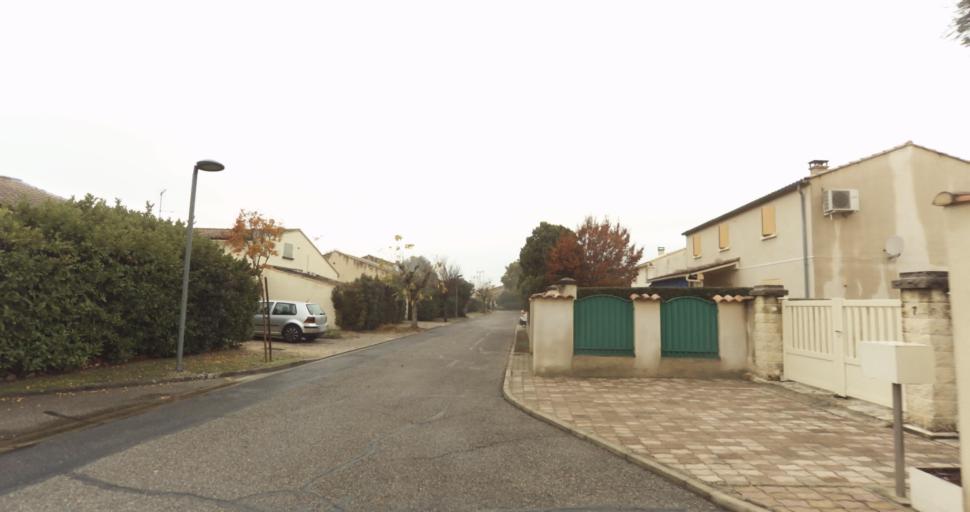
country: FR
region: Provence-Alpes-Cote d'Azur
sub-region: Departement des Bouches-du-Rhone
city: Rognonas
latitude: 43.9011
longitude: 4.8099
